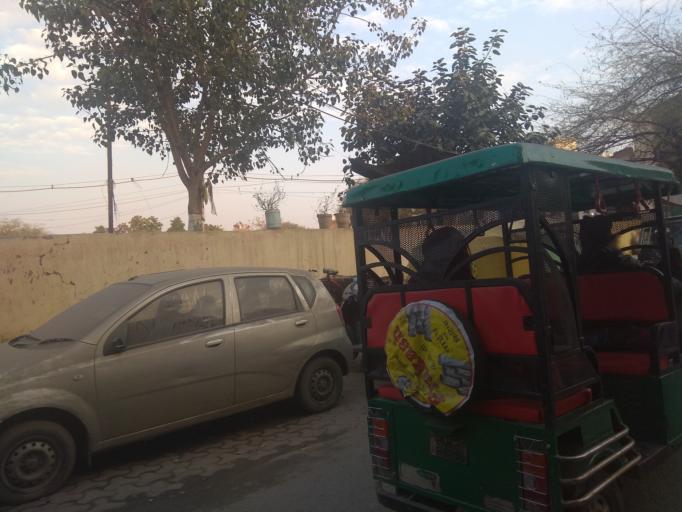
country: IN
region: NCT
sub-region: West Delhi
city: Nangloi Jat
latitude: 28.6321
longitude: 77.0763
